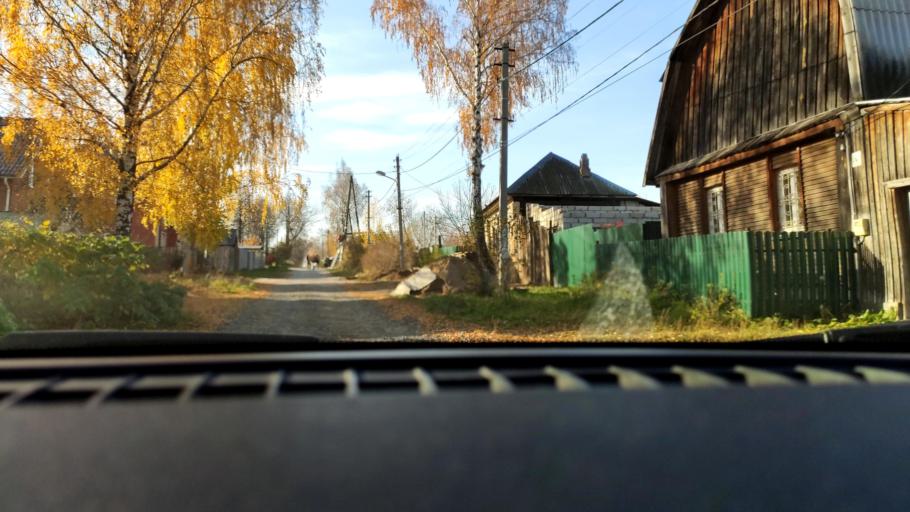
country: RU
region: Perm
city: Perm
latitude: 58.0251
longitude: 56.3162
